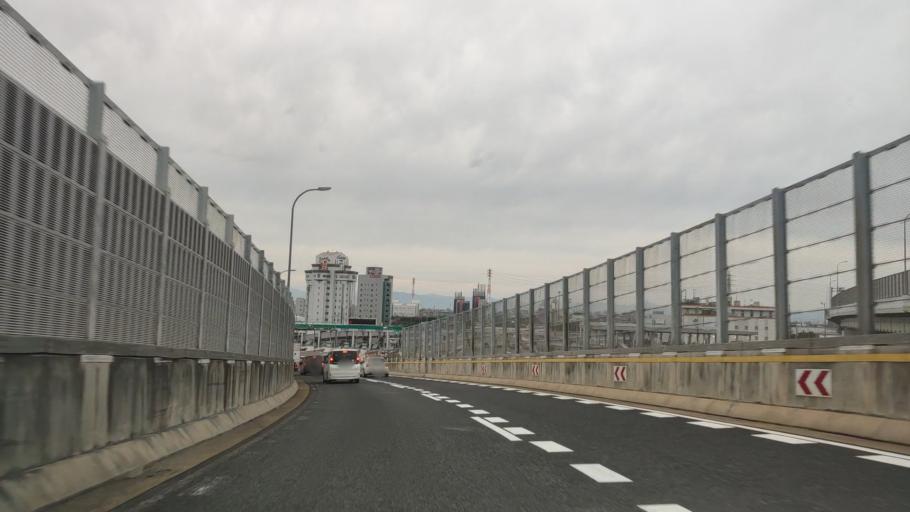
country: JP
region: Aichi
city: Iwakura
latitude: 35.2702
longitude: 136.8319
